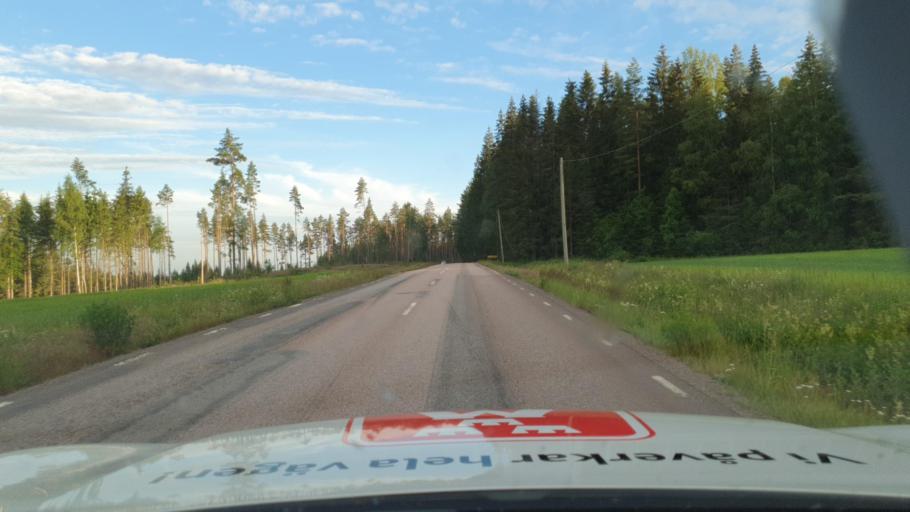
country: SE
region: Vaermland
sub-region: Karlstads Kommun
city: Skattkarr
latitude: 59.4402
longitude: 13.8361
